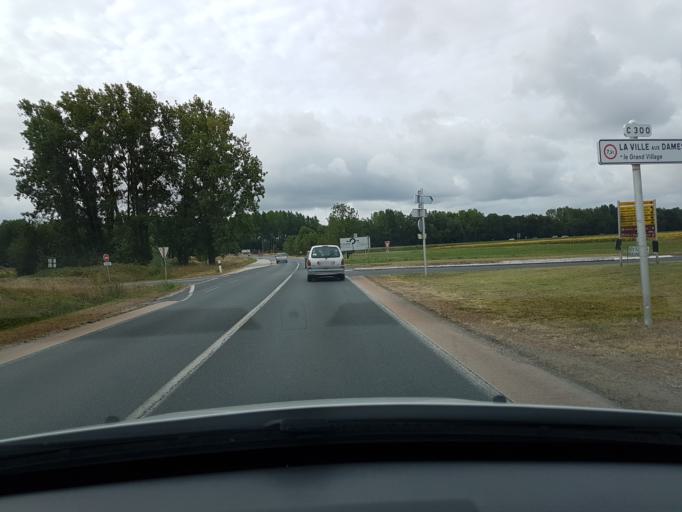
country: FR
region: Centre
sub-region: Departement d'Indre-et-Loire
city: Larcay
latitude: 47.3840
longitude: 0.7845
